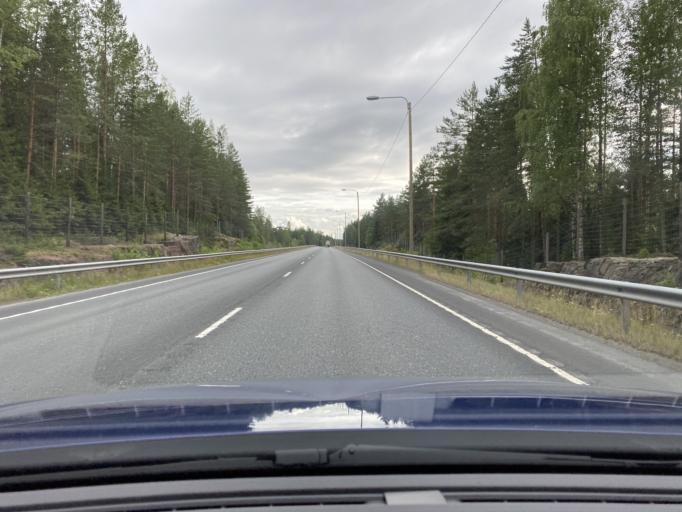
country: FI
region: Pirkanmaa
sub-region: Tampere
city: Kangasala
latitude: 61.5661
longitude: 24.1020
